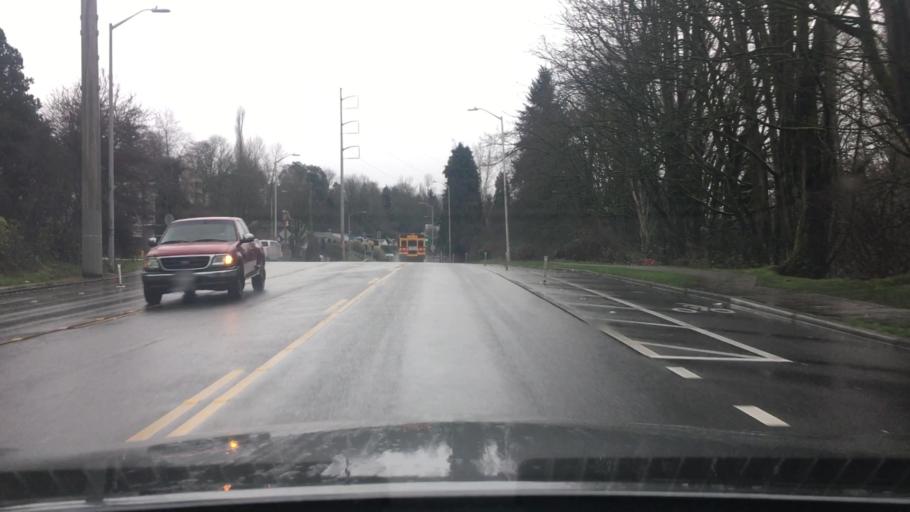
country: US
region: Washington
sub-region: King County
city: White Center
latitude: 47.5353
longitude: -122.3611
